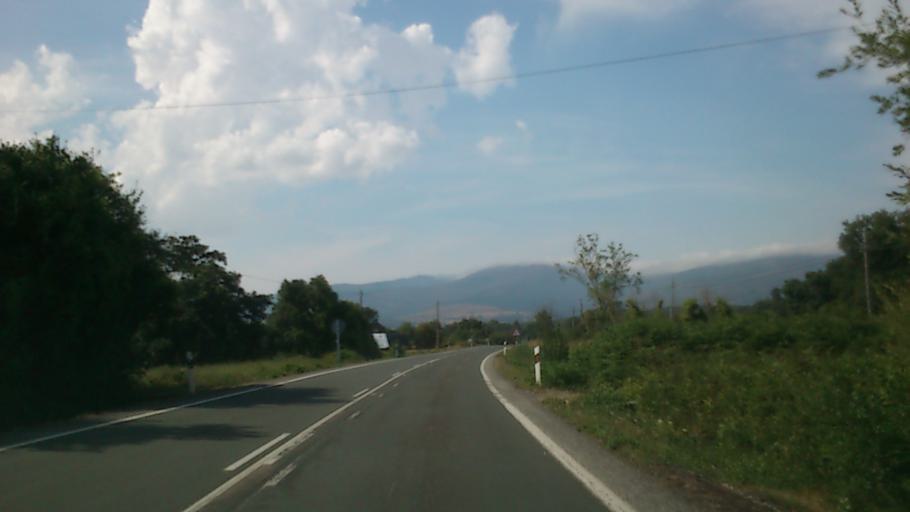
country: ES
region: Castille and Leon
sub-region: Provincia de Burgos
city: Espinosa de los Monteros
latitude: 43.0546
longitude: -3.4912
